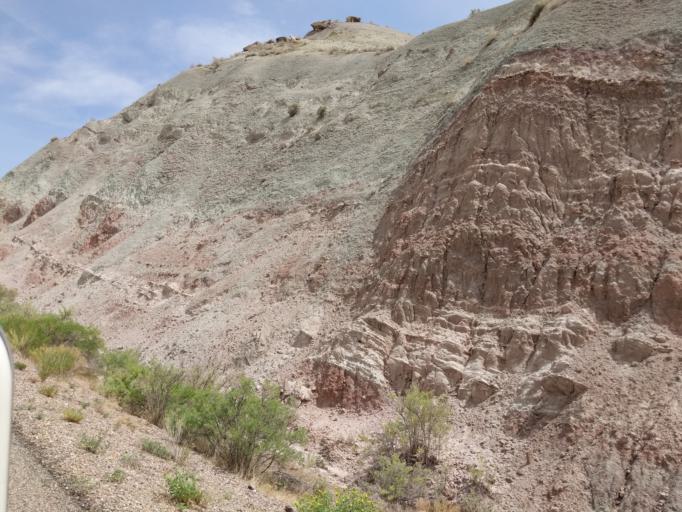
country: US
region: Utah
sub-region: Uintah County
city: Naples
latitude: 40.4412
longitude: -109.3023
